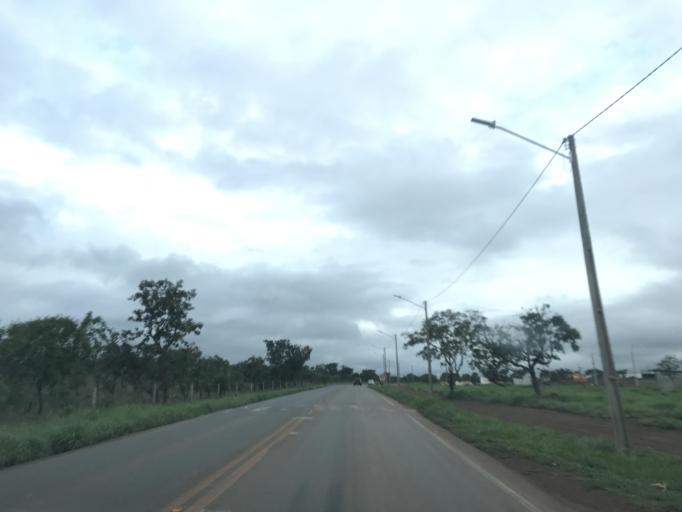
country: BR
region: Goias
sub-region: Luziania
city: Luziania
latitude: -16.2638
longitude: -47.9750
